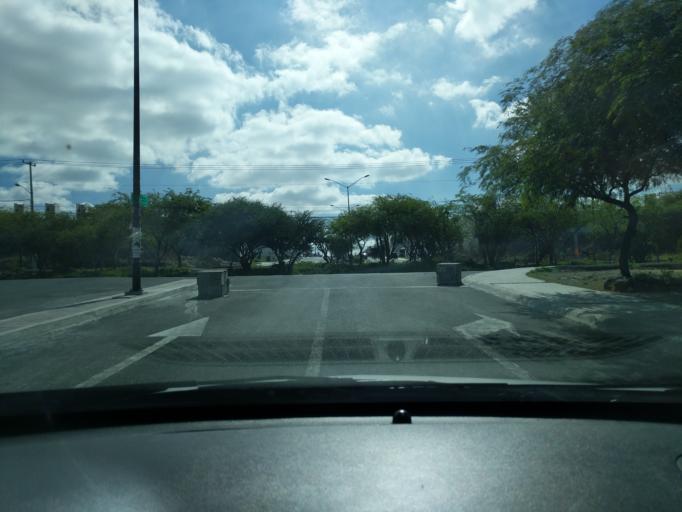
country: MX
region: Queretaro
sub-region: Queretaro
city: Patria Nueva
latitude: 20.6399
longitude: -100.4914
